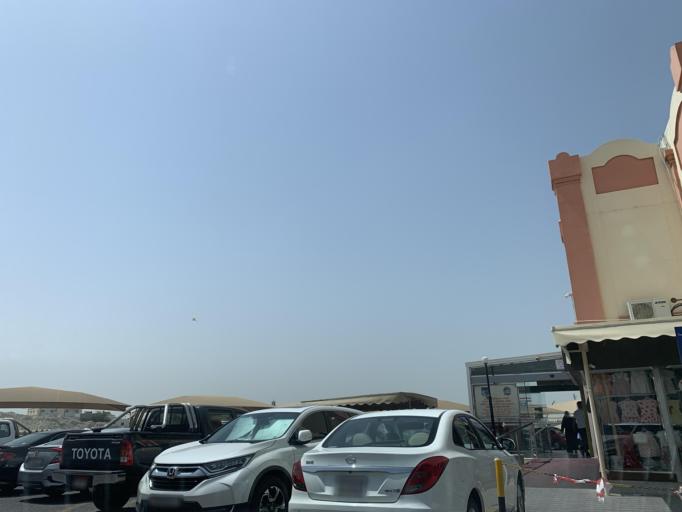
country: BH
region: Manama
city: Jidd Hafs
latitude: 26.1975
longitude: 50.5588
